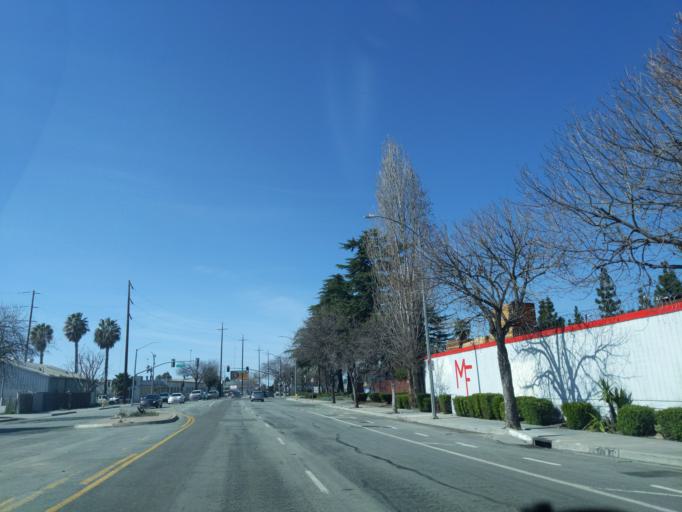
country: US
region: California
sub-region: Santa Clara County
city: Seven Trees
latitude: 37.3149
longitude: -121.8616
